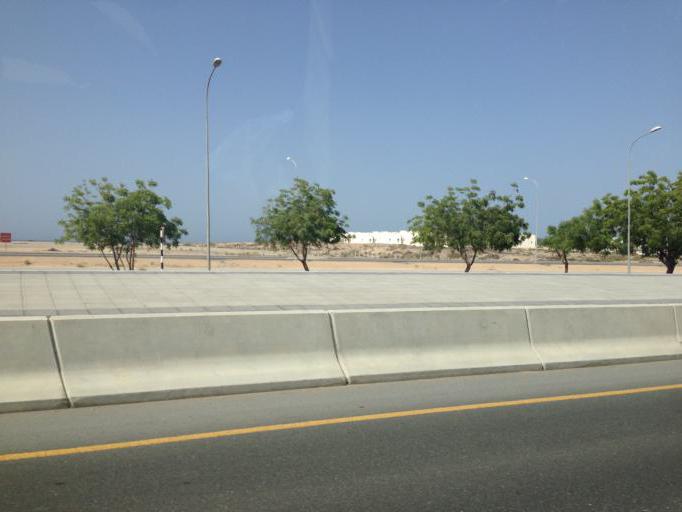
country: OM
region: Muhafazat Masqat
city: Bawshar
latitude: 23.6047
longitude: 58.3261
